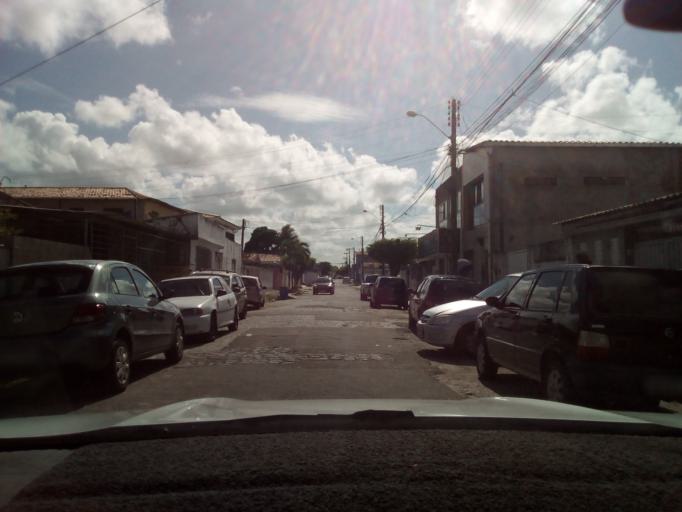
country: BR
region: Paraiba
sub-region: Joao Pessoa
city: Joao Pessoa
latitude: -7.1285
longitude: -34.8792
